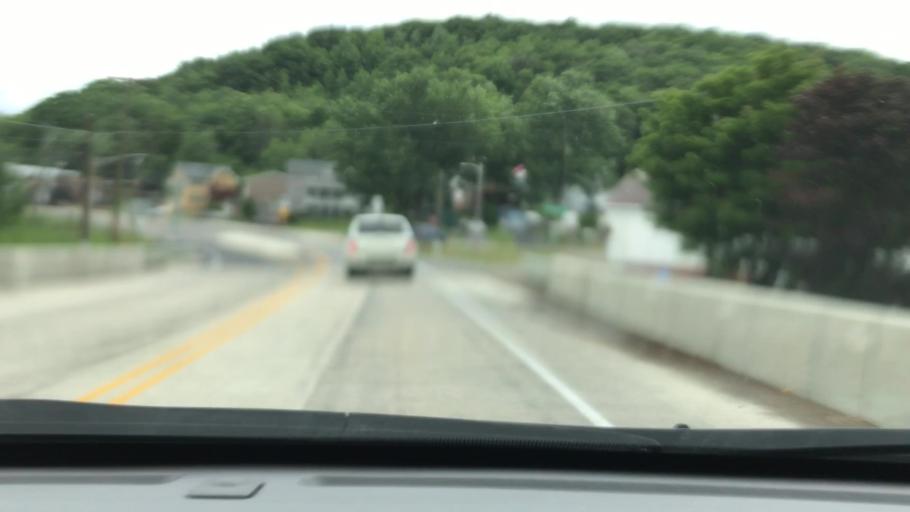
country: US
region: Pennsylvania
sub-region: Elk County
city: Johnsonburg
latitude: 41.4793
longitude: -78.6698
